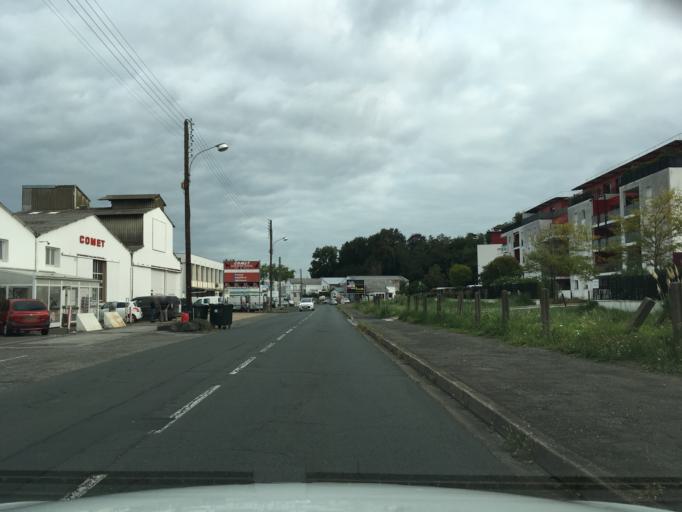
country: FR
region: Aquitaine
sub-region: Departement des Pyrenees-Atlantiques
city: Bayonne
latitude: 43.4948
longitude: -1.4915
